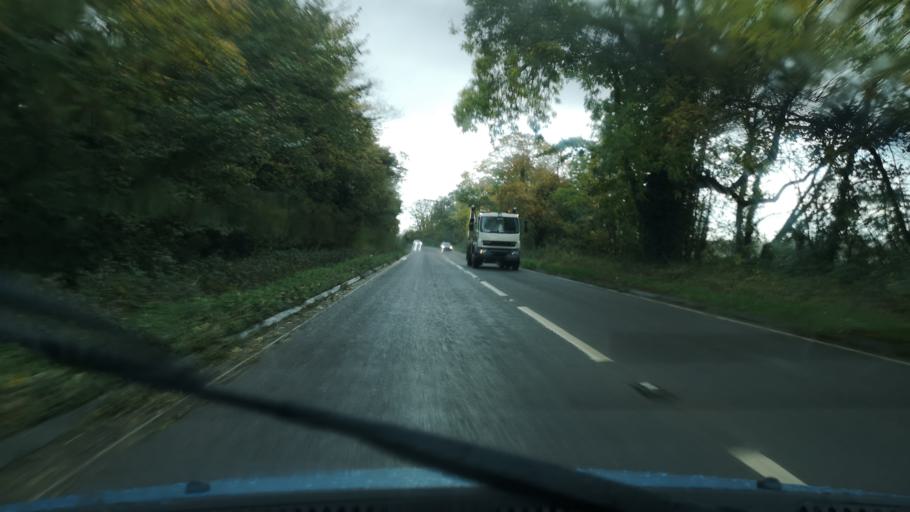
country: GB
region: England
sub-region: North Lincolnshire
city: Crowle
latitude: 53.5869
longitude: -0.8234
